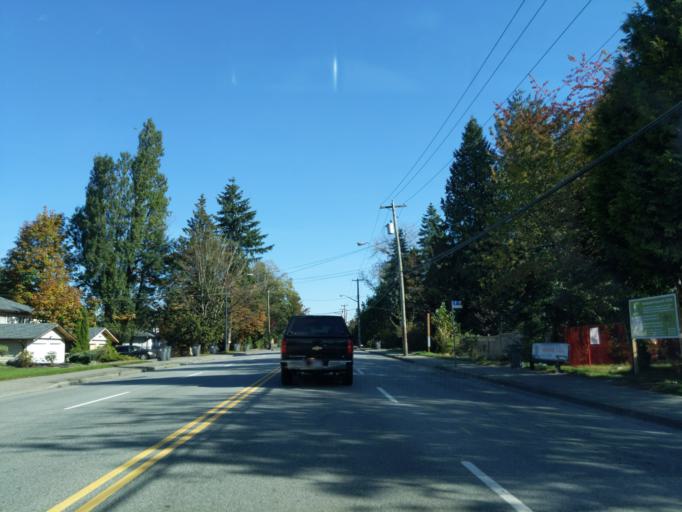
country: CA
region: British Columbia
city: New Westminster
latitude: 49.1988
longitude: -122.8396
